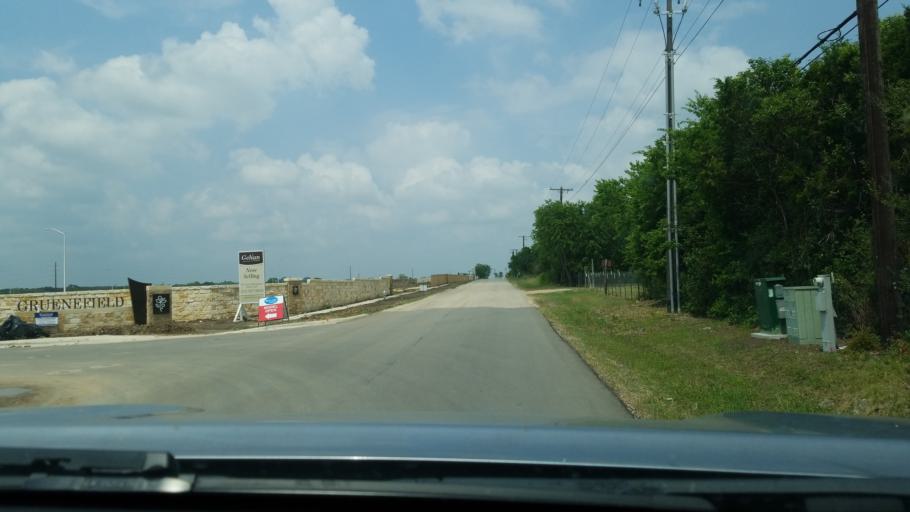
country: US
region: Texas
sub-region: Comal County
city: New Braunfels
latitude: 29.7466
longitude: -98.0946
